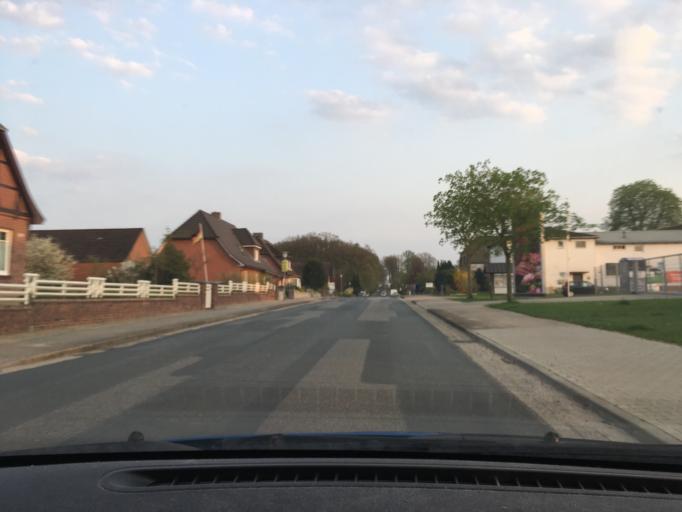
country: DE
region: Lower Saxony
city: Amelinghausen
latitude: 53.1362
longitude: 10.2138
